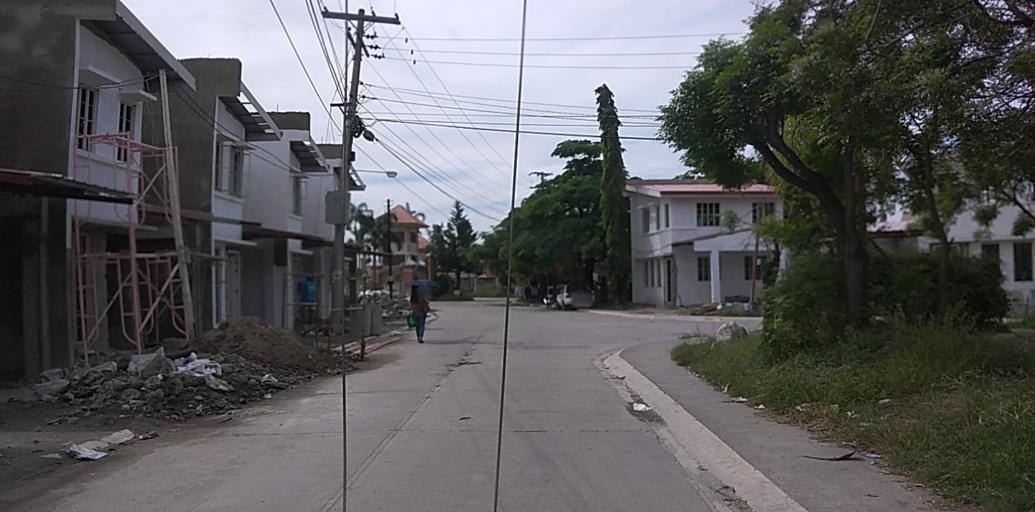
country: PH
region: Central Luzon
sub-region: Province of Pampanga
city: Manibaug Pasig
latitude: 15.1131
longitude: 120.5623
